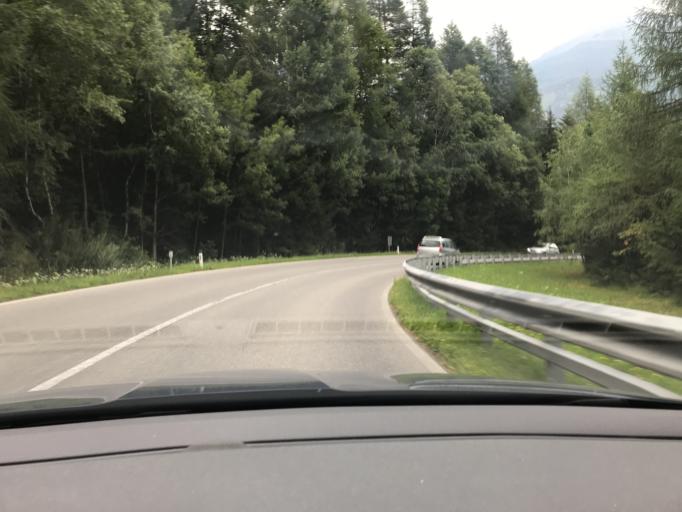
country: AT
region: Tyrol
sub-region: Politischer Bezirk Lienz
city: Hopfgarten in Defereggen
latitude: 46.9249
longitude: 12.5682
